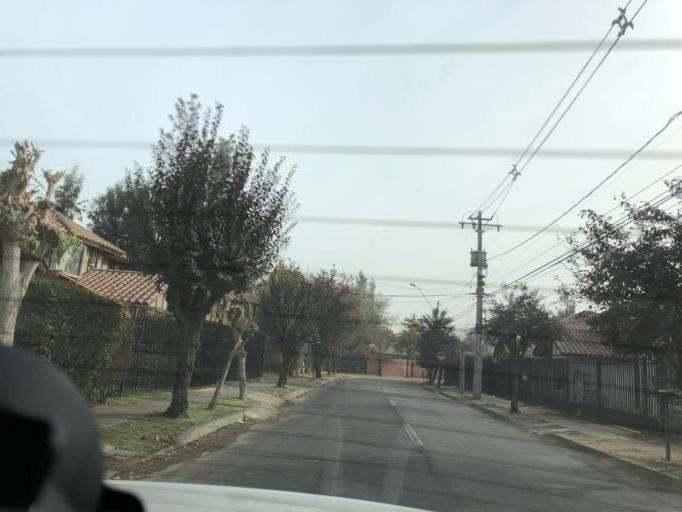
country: CL
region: Santiago Metropolitan
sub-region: Provincia de Cordillera
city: Puente Alto
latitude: -33.5489
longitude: -70.5656
